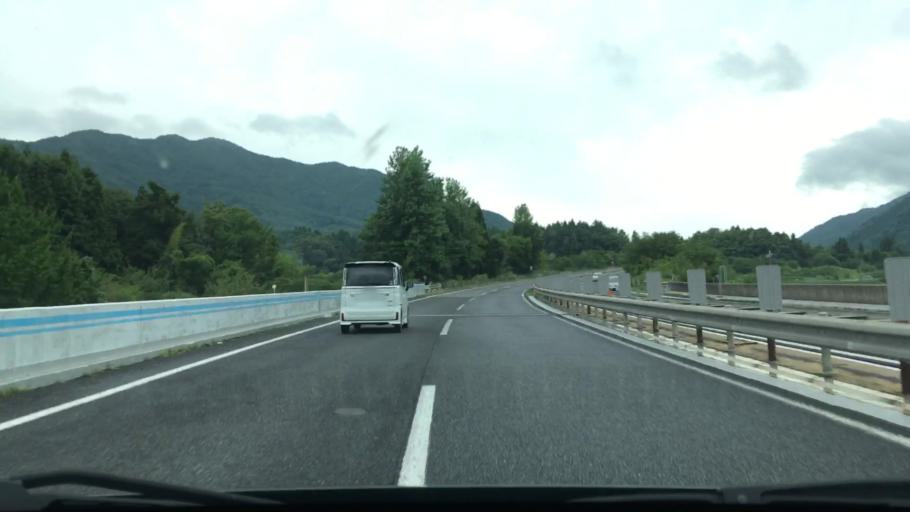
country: JP
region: Hiroshima
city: Hiroshima-shi
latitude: 34.6432
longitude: 132.5171
